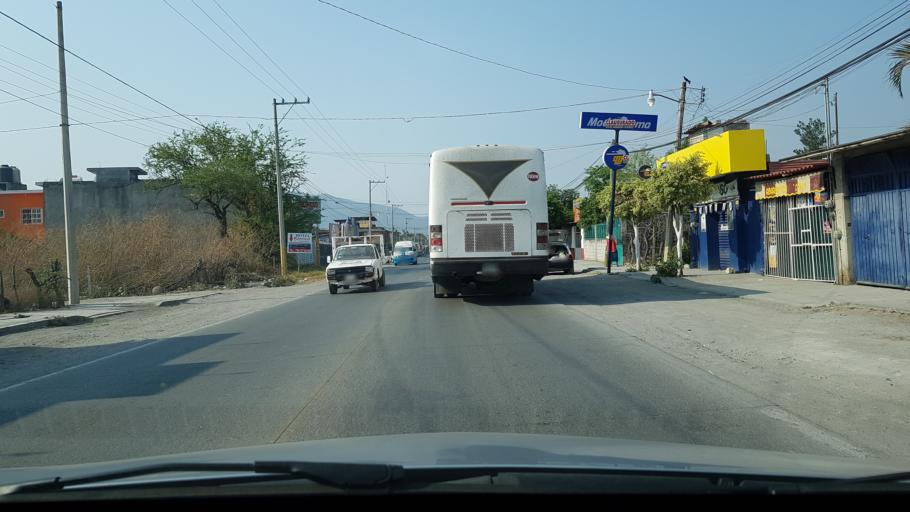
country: MX
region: Morelos
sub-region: Tlaquiltenango
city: Alfredo V. Bonfil (Chacampalco)
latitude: 18.6474
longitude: -99.1561
